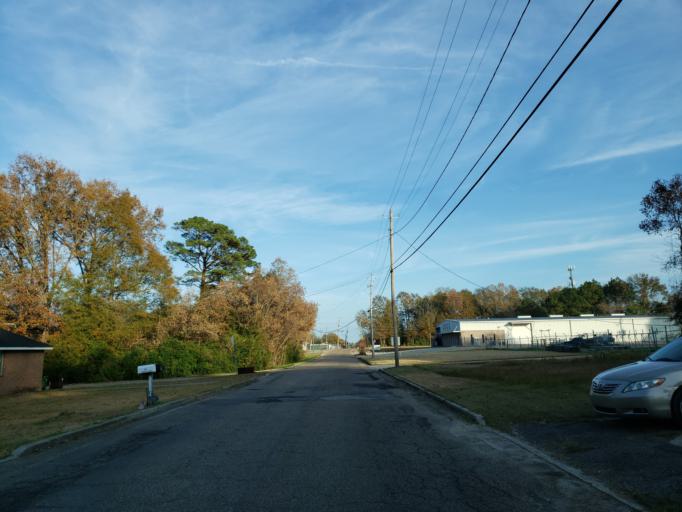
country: US
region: Mississippi
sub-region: Forrest County
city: Hattiesburg
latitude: 31.2992
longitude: -89.3121
